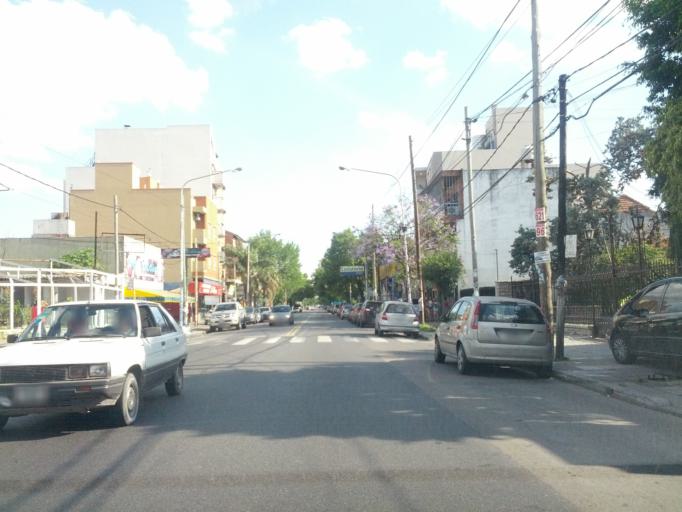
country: AR
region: Buenos Aires
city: San Justo
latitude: -34.6535
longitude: -58.5633
